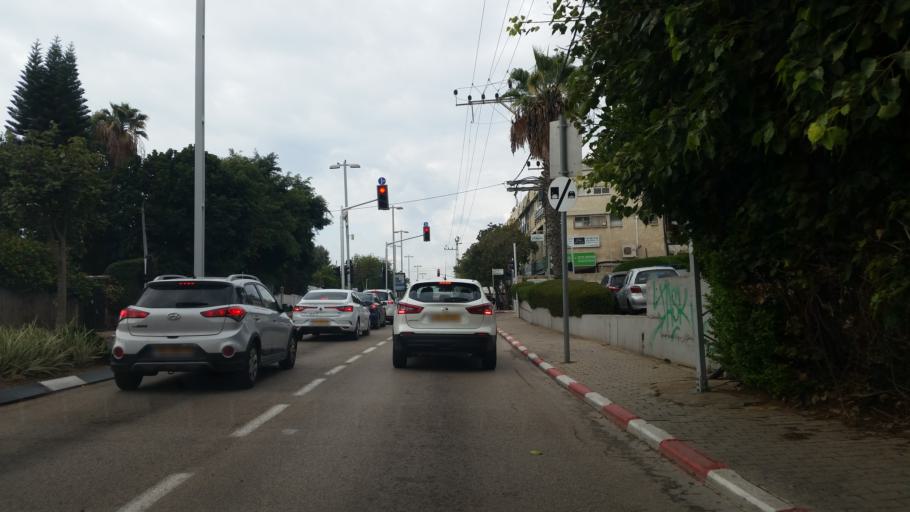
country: IL
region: Tel Aviv
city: Kefar Shemaryahu
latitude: 32.1796
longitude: 34.8200
